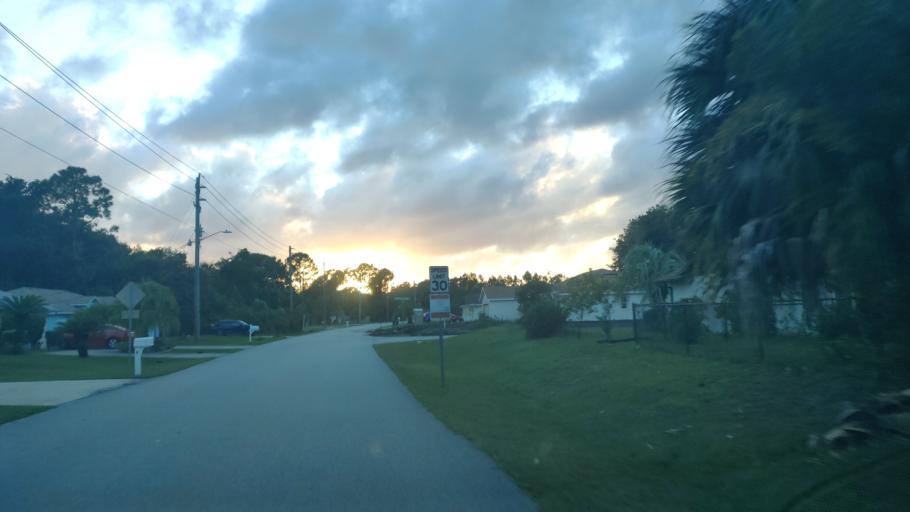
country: US
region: Florida
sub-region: Flagler County
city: Bunnell
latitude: 29.5215
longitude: -81.2256
